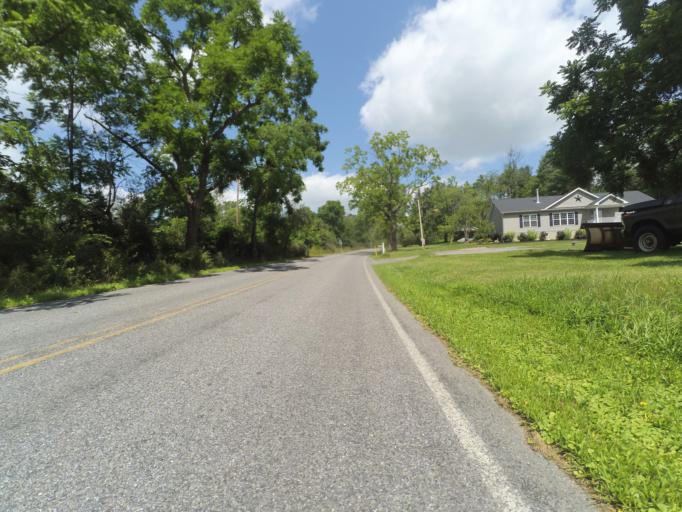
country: US
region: Pennsylvania
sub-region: Centre County
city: Stormstown
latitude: 40.7787
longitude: -78.0432
